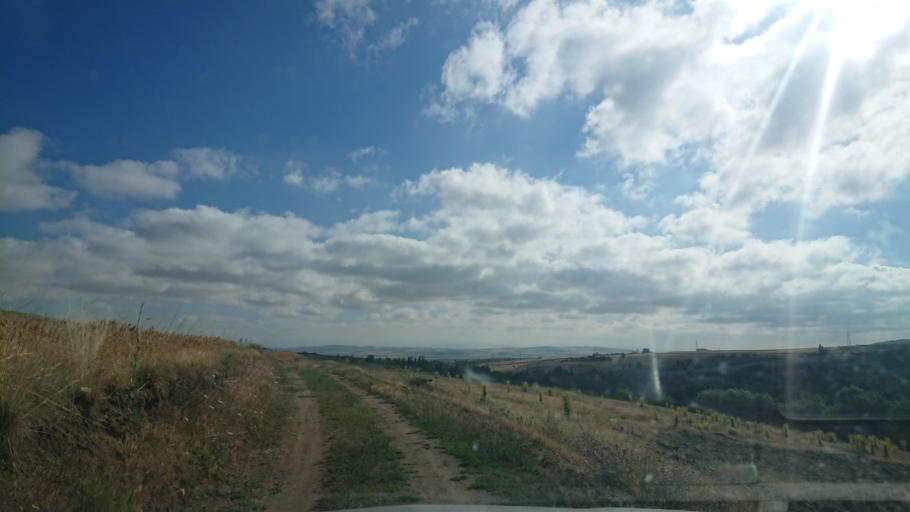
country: TR
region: Aksaray
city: Agacoren
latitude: 38.8490
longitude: 33.9275
